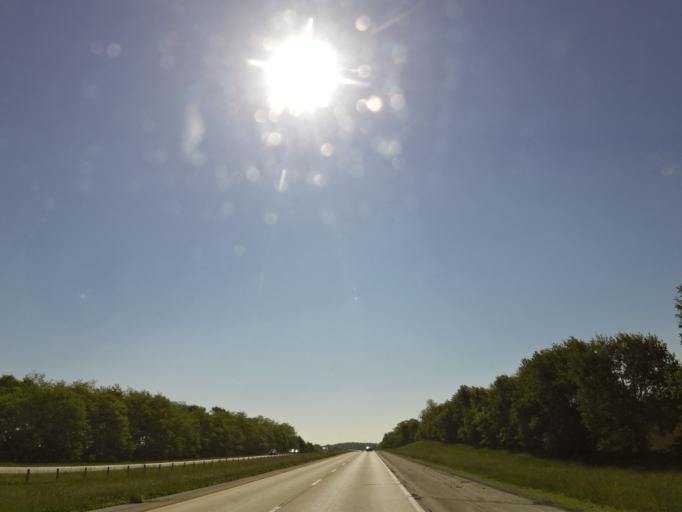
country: US
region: Kentucky
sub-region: Woodford County
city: Midway
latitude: 38.1662
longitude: -84.7532
